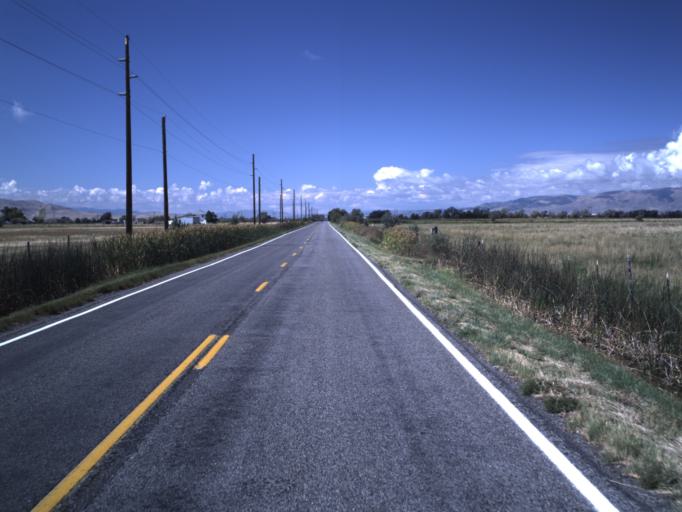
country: US
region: Utah
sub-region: Utah County
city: Spanish Fork
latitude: 40.1586
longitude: -111.6651
